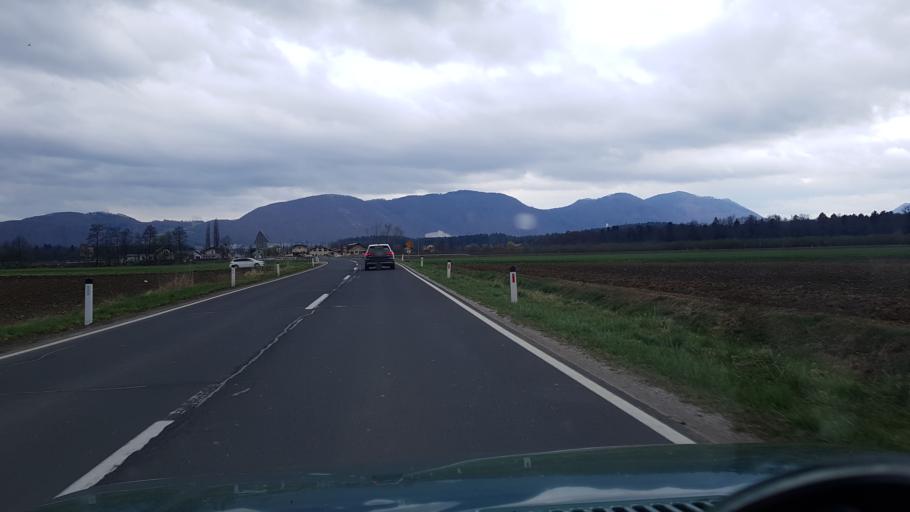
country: SI
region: Oplotnica
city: Oplotnica
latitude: 46.3540
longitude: 15.4876
